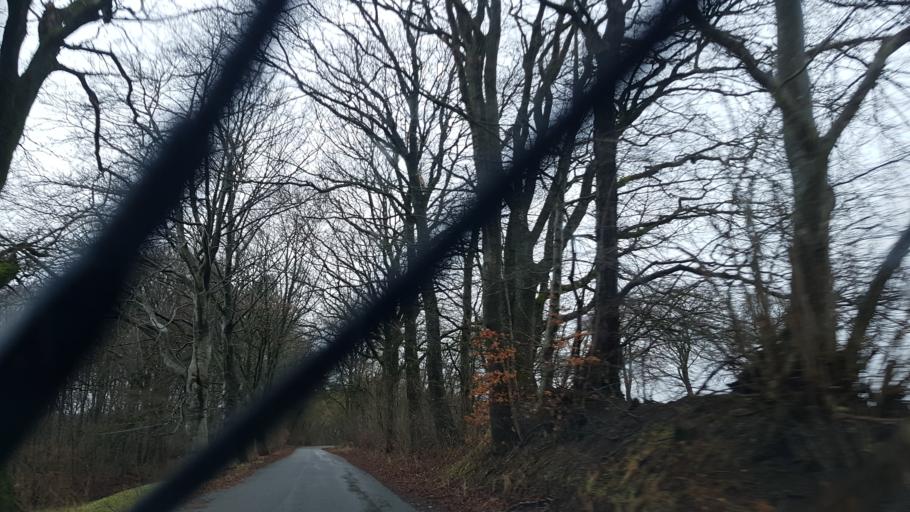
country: DK
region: South Denmark
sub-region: Kolding Kommune
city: Vamdrup
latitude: 55.3783
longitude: 9.2426
